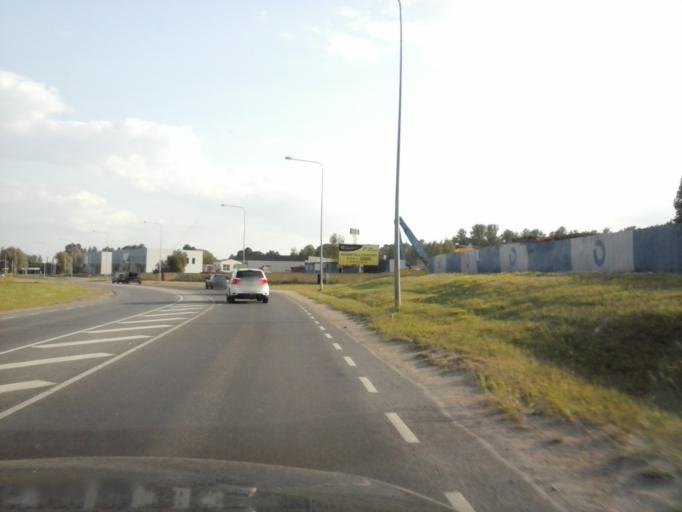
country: EE
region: Tartu
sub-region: Tartu linn
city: Tartu
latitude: 58.3583
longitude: 26.7409
